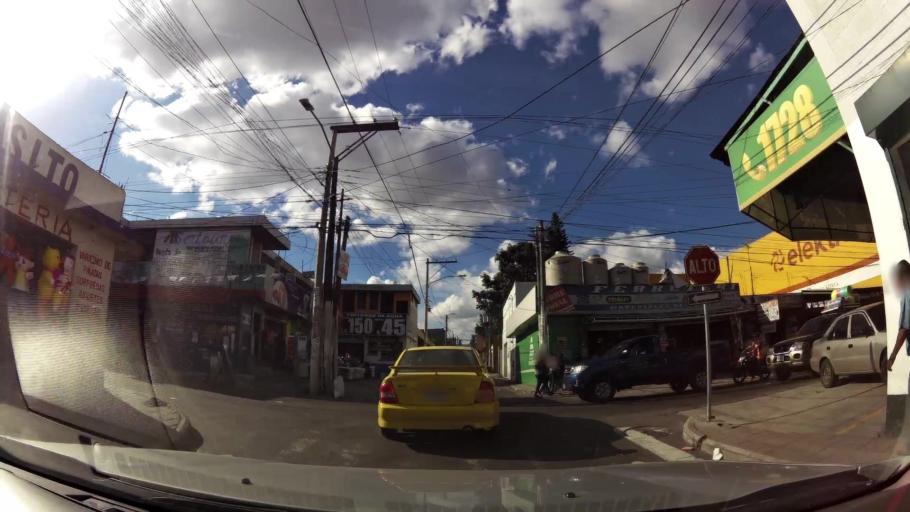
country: GT
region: Guatemala
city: Villa Nueva
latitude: 14.5256
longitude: -90.5894
